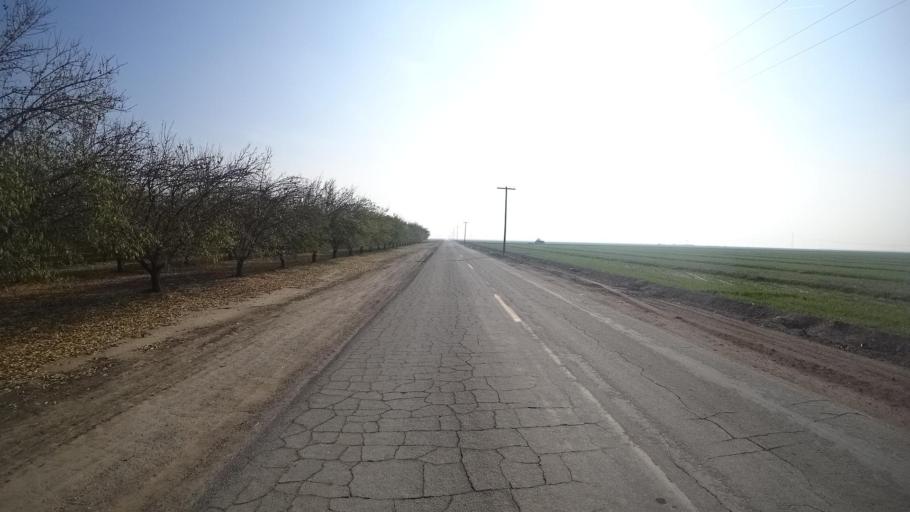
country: US
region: California
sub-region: Kern County
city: Greenfield
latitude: 35.1919
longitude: -119.0436
